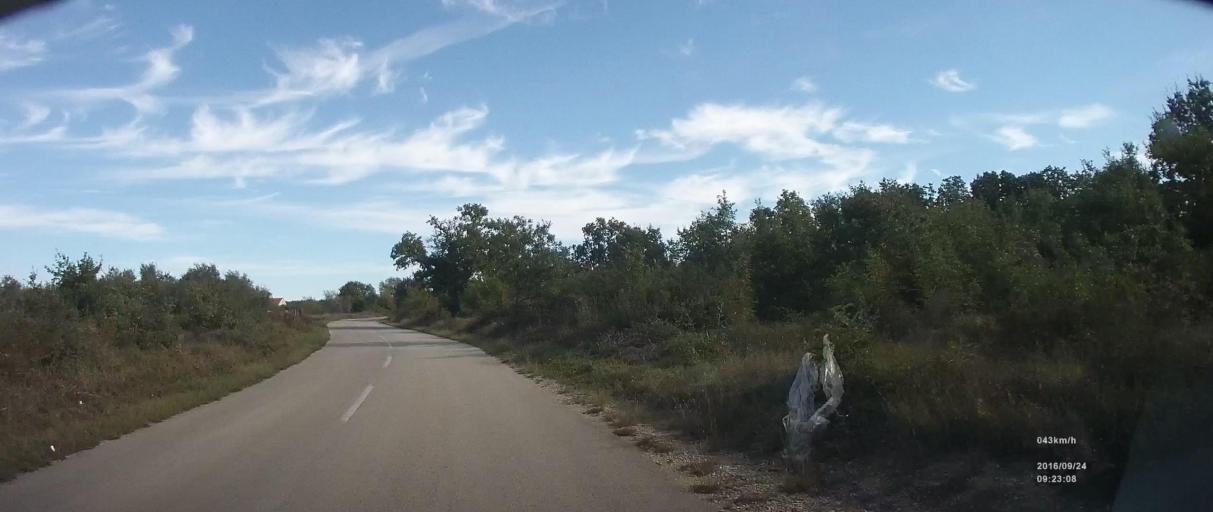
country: HR
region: Zadarska
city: Polaca
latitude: 44.0722
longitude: 15.4749
